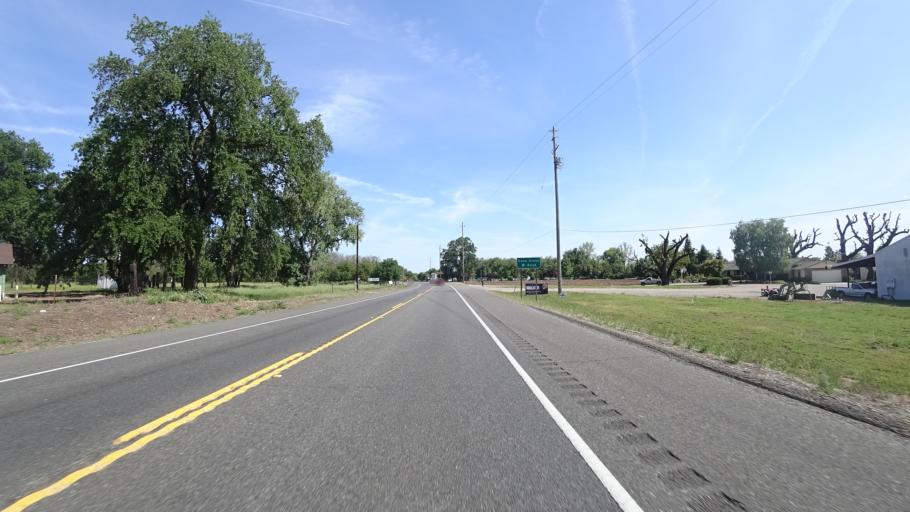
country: US
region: California
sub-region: Tehama County
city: Red Bluff
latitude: 40.1706
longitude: -122.1633
